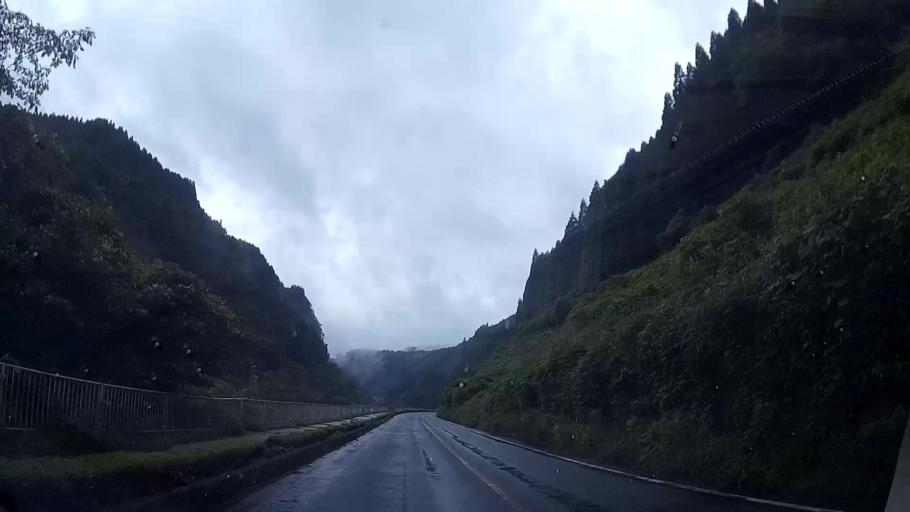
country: JP
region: Oita
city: Tsukawaki
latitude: 33.1779
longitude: 131.0361
